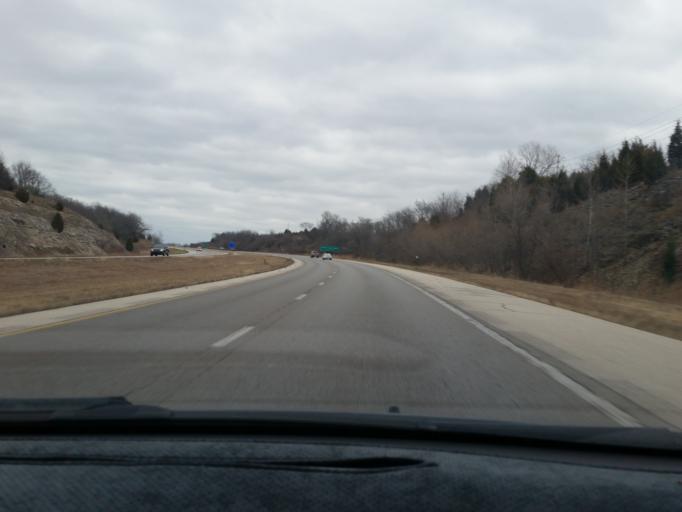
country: US
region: Kansas
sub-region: Johnson County
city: De Soto
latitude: 38.9477
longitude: -94.8995
